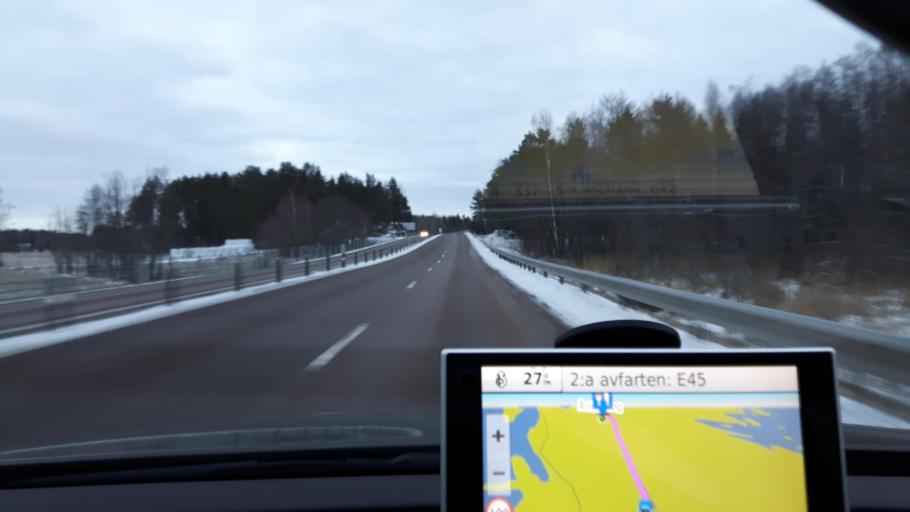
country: SE
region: Vaestra Goetaland
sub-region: Melleruds Kommun
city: Mellerud
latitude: 58.8428
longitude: 12.5471
